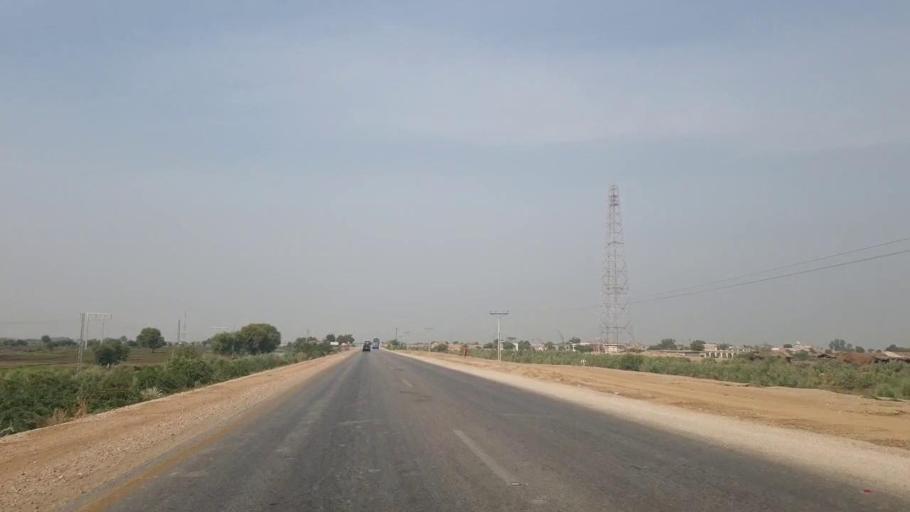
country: PK
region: Sindh
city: Sann
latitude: 26.0849
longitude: 68.0926
